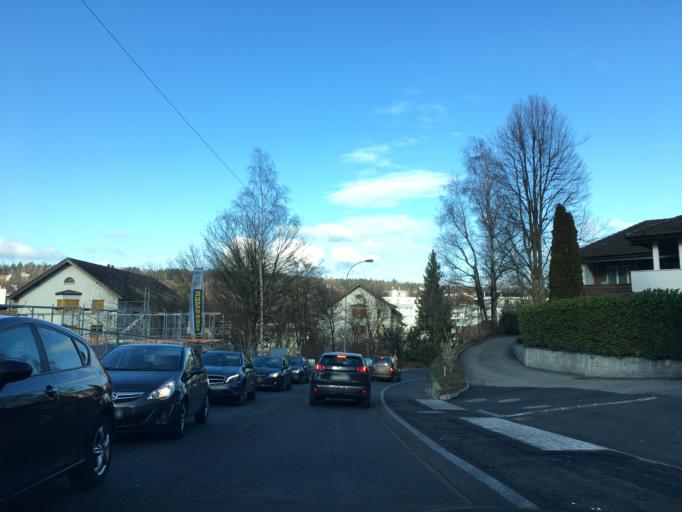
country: CH
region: Lucerne
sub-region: Lucerne-Land District
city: Ebikon
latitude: 47.0757
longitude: 8.3377
